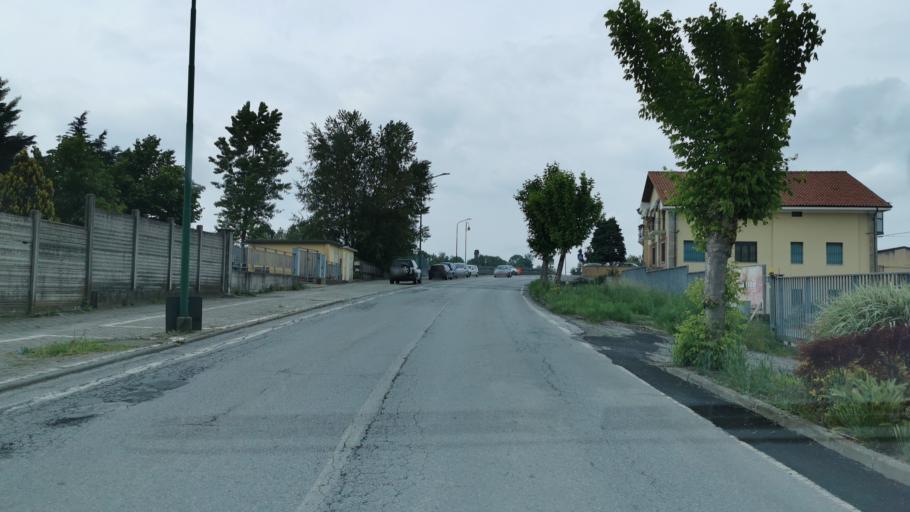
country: IT
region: Piedmont
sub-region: Provincia di Cuneo
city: Villafalletto
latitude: 44.5493
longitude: 7.5392
